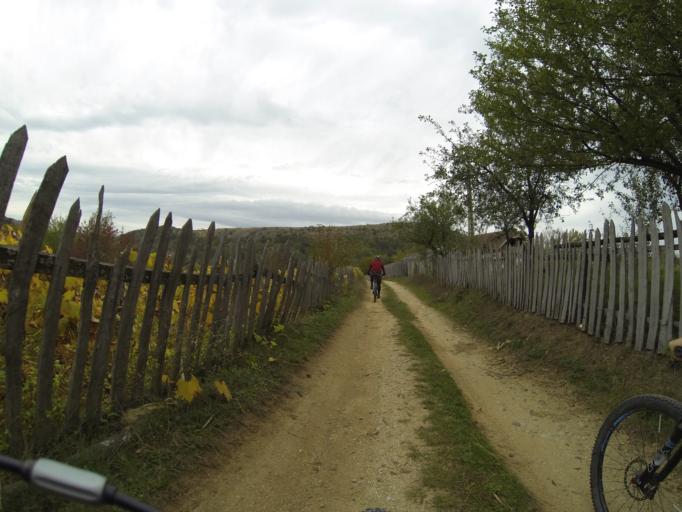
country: RO
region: Gorj
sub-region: Comuna Tismana
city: Sohodol
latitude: 45.0580
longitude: 22.8888
